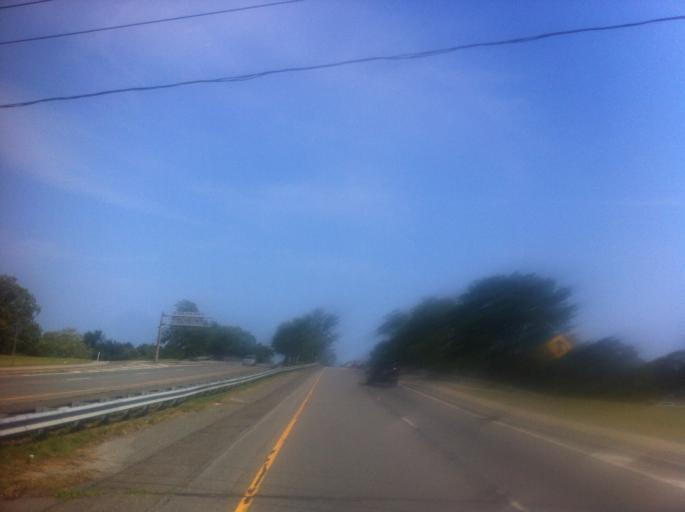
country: US
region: New York
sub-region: Suffolk County
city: North Lindenhurst
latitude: 40.7126
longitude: -73.3729
